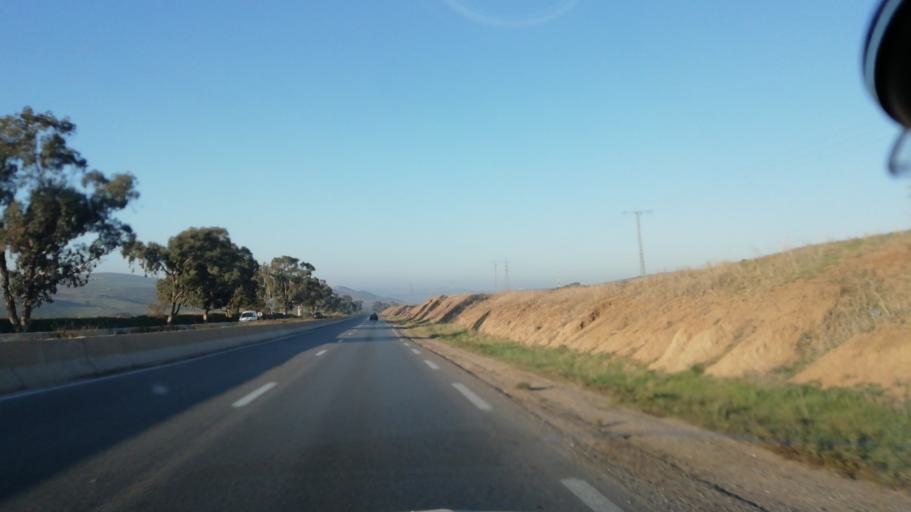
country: DZ
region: Ain Temouchent
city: Beni Saf
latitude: 35.2324
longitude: -1.3529
